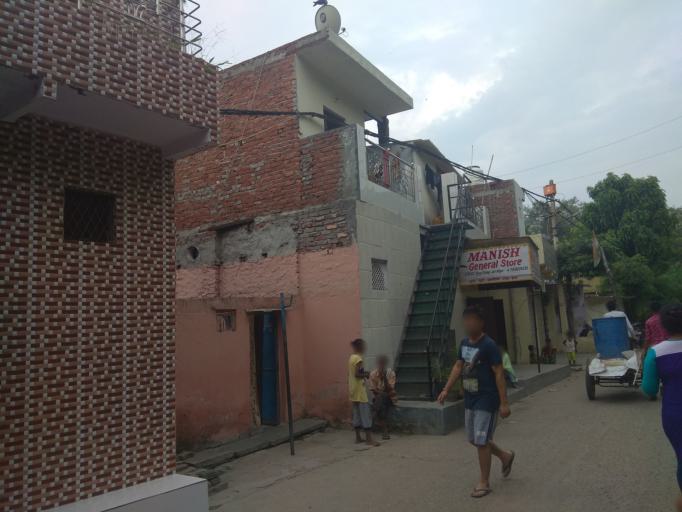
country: IN
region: NCT
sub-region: New Delhi
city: New Delhi
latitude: 28.5746
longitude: 77.2517
